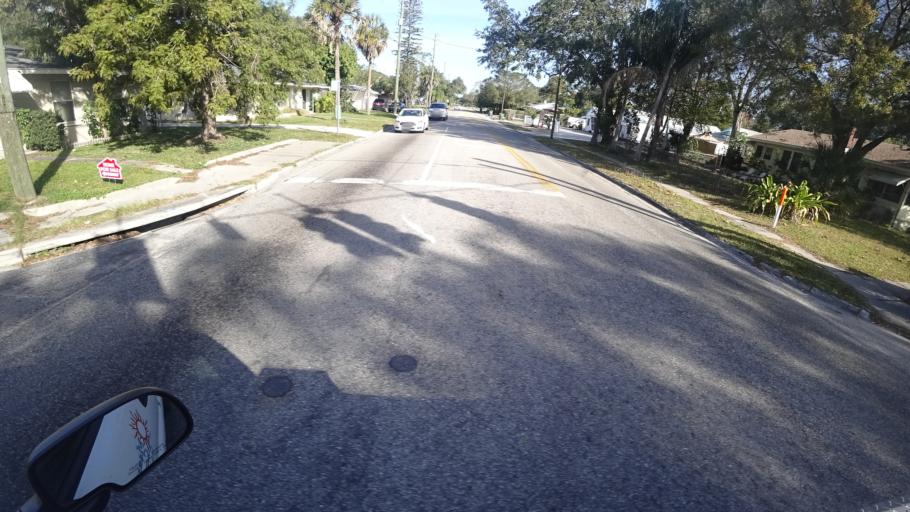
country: US
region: Florida
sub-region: Manatee County
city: Bradenton
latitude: 27.4847
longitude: -82.5875
